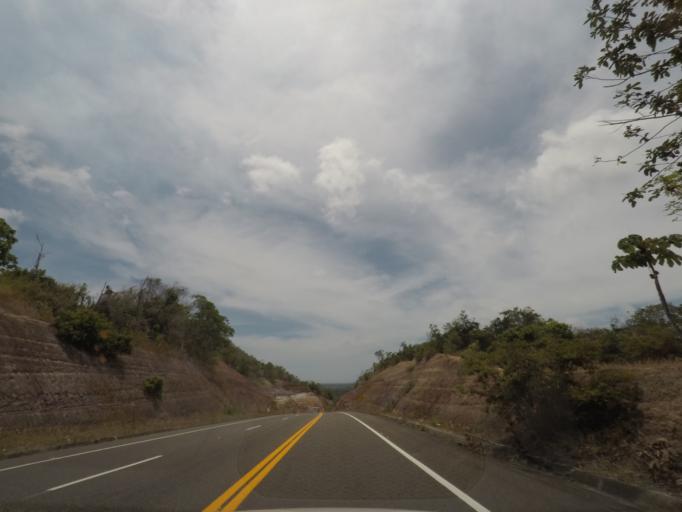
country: BR
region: Bahia
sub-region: Conde
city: Conde
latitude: -11.7630
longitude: -37.5903
